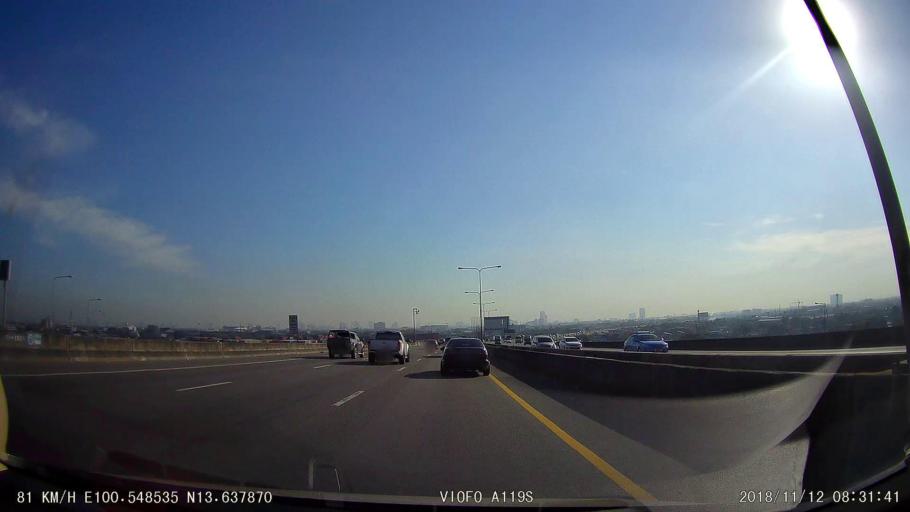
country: TH
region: Samut Prakan
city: Phra Pradaeng
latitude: 13.6382
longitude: 100.5493
